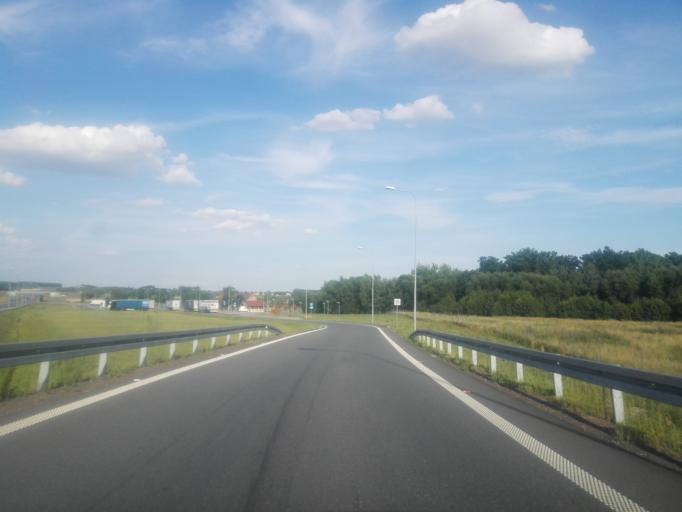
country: PL
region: Lower Silesian Voivodeship
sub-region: Powiat olesnicki
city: Sycow
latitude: 51.2941
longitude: 17.7308
